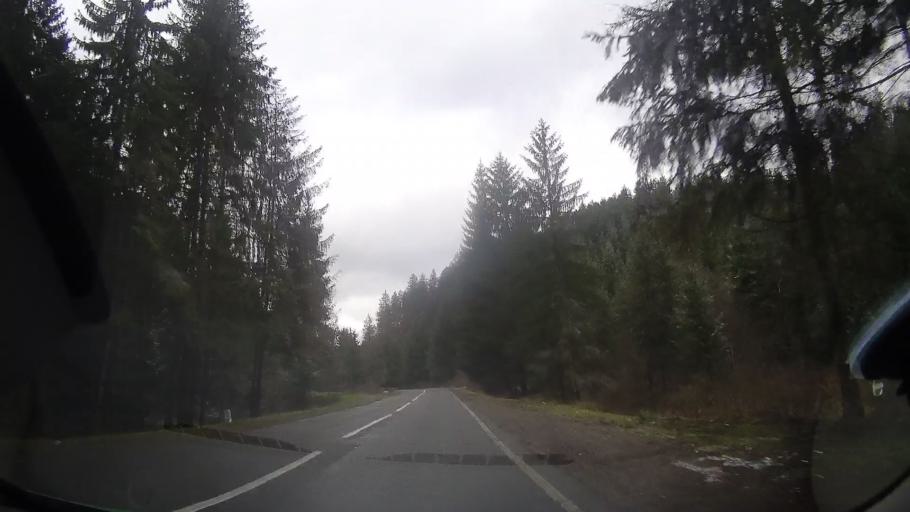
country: RO
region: Cluj
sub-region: Comuna Calatele
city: Calatele
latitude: 46.7501
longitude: 23.0137
